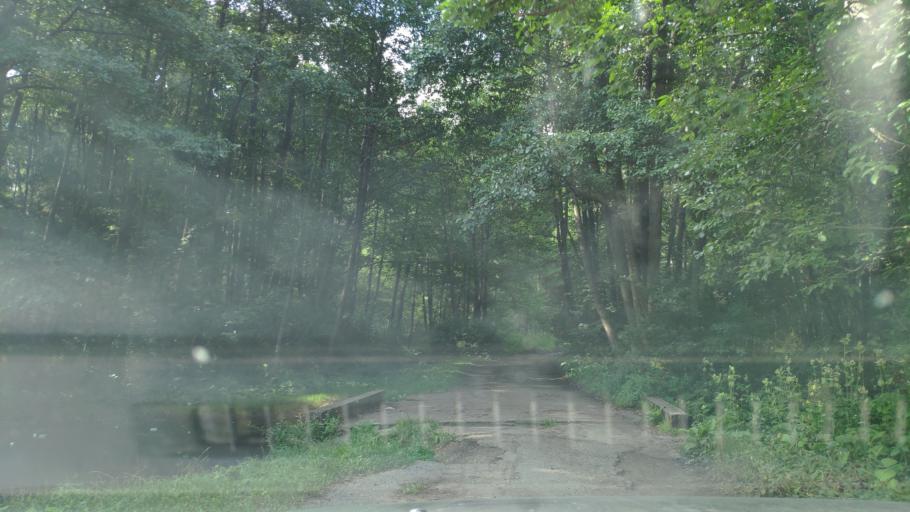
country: BY
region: Minsk
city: Zaslawye
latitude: 53.9747
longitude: 27.2899
